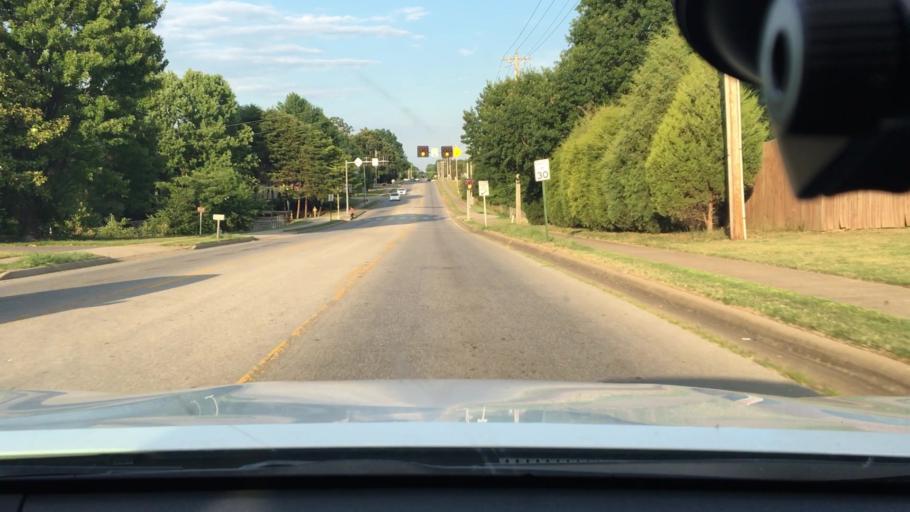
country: US
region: Arkansas
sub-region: Benton County
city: Rogers
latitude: 36.3416
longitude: -94.1593
